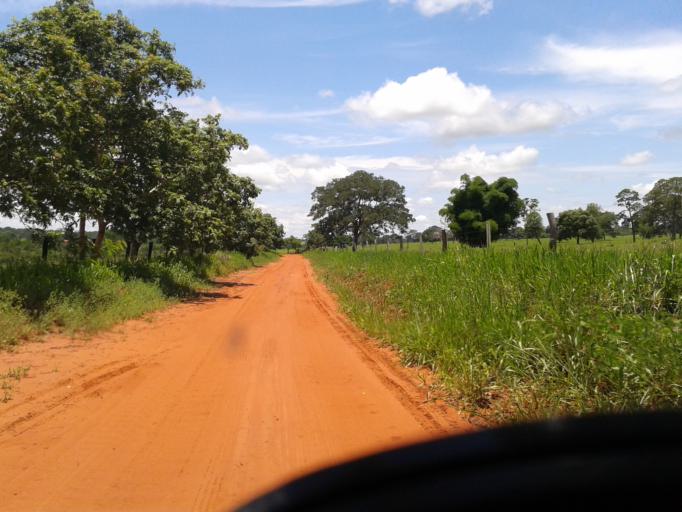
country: BR
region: Minas Gerais
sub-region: Santa Vitoria
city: Santa Vitoria
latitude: -18.9464
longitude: -49.8621
